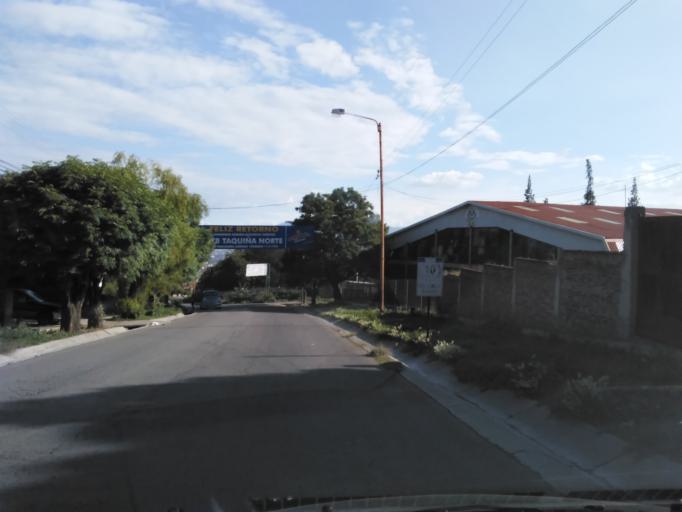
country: BO
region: Cochabamba
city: Cochabamba
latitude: -17.3361
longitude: -66.1834
